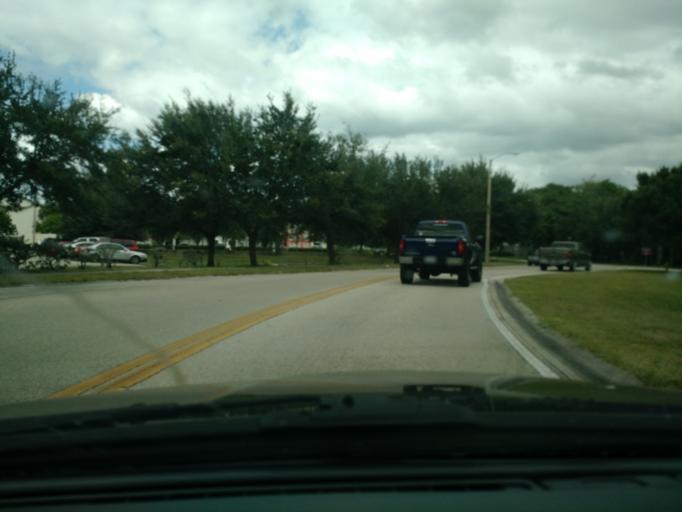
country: US
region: Florida
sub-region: Lee County
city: Pine Manor
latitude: 26.5828
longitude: -81.8771
